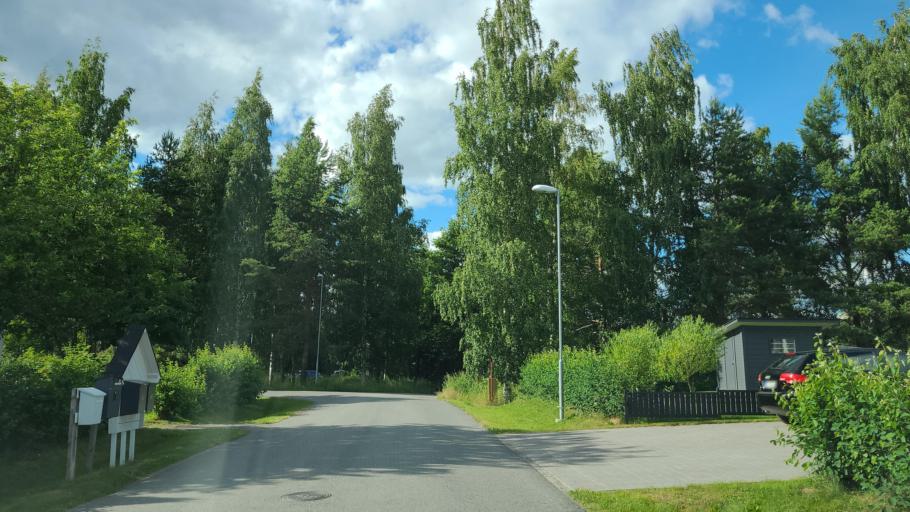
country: FI
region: Northern Savo
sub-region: Kuopio
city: Kuopio
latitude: 62.9280
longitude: 27.6281
